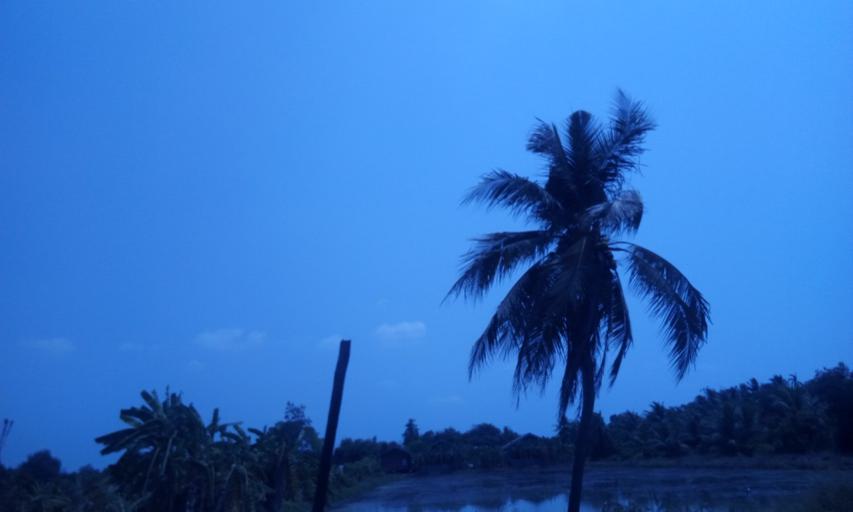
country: TH
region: Chachoengsao
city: Bang Nam Priao
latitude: 13.8743
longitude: 100.9675
